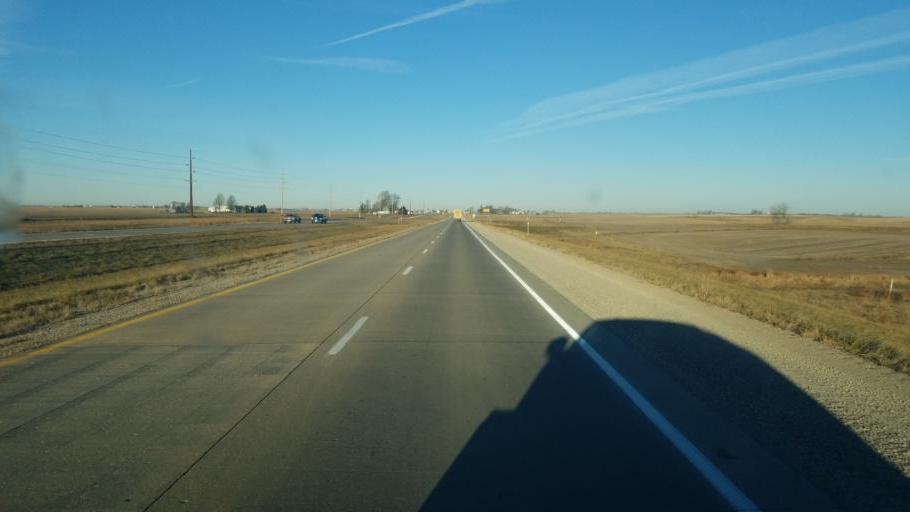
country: US
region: Iowa
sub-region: Mahaska County
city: Oskaloosa
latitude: 41.3604
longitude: -92.7763
